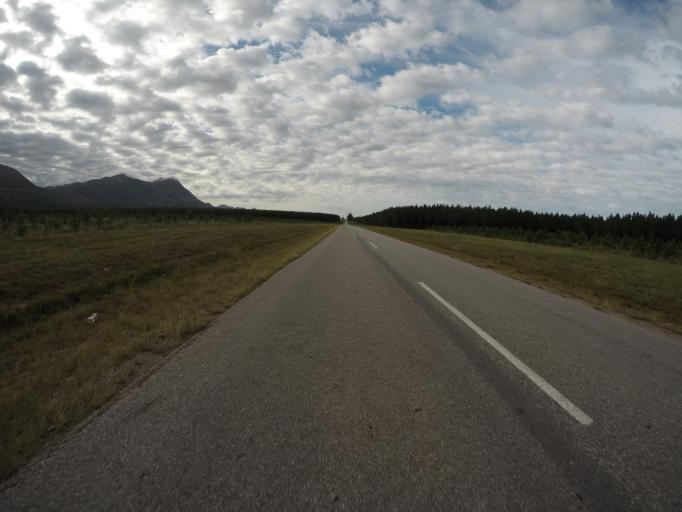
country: ZA
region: Eastern Cape
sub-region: Cacadu District Municipality
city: Kareedouw
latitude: -34.0311
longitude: 24.3824
